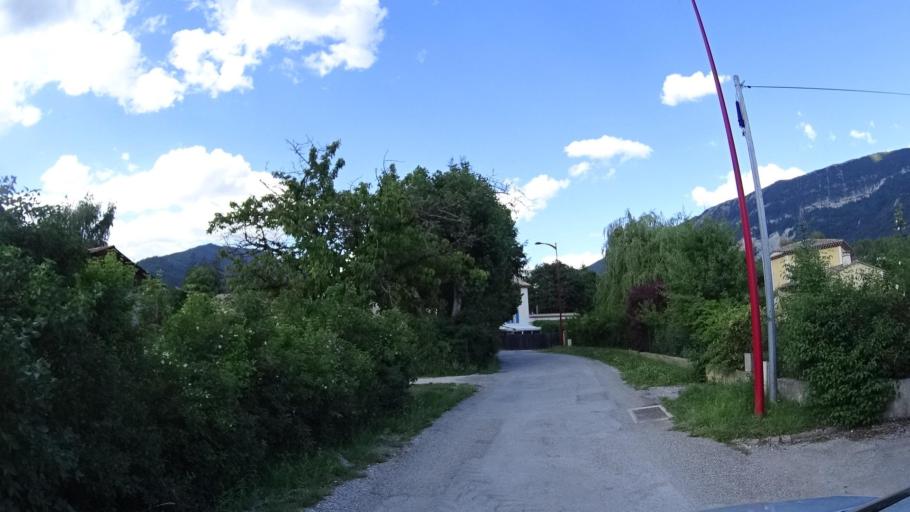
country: FR
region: Provence-Alpes-Cote d'Azur
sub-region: Departement des Alpes-de-Haute-Provence
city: Castellane
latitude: 43.9673
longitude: 6.5129
